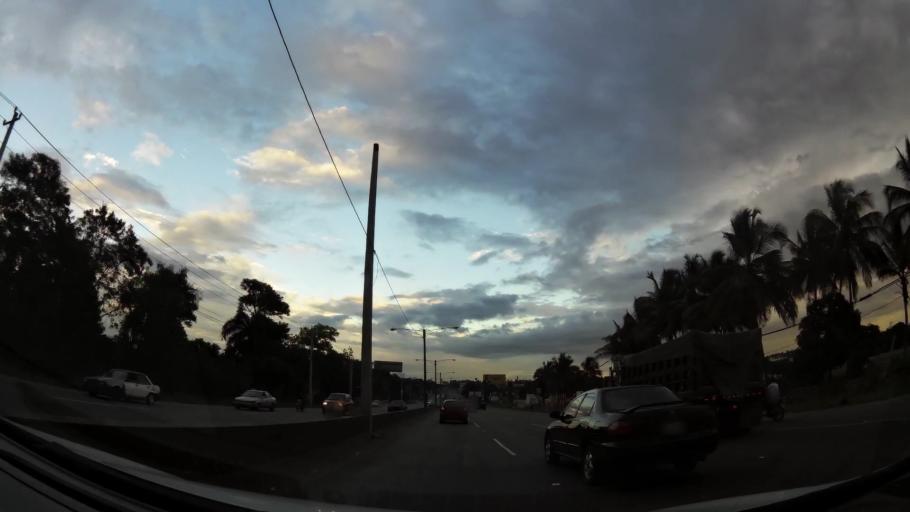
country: DO
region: Santo Domingo
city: Santo Domingo Oeste
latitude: 18.5401
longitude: -70.0316
